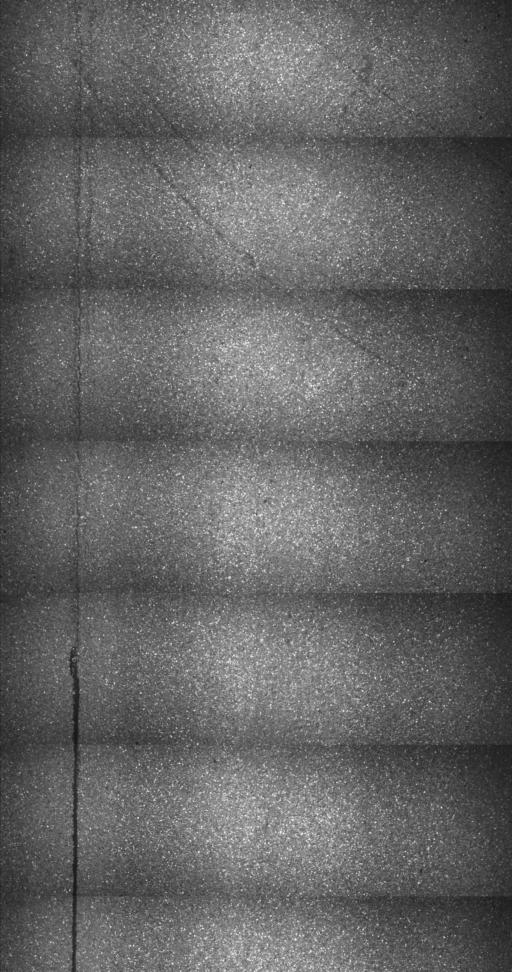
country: US
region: Vermont
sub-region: Rutland County
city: Fair Haven
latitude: 43.6707
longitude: -73.2895
